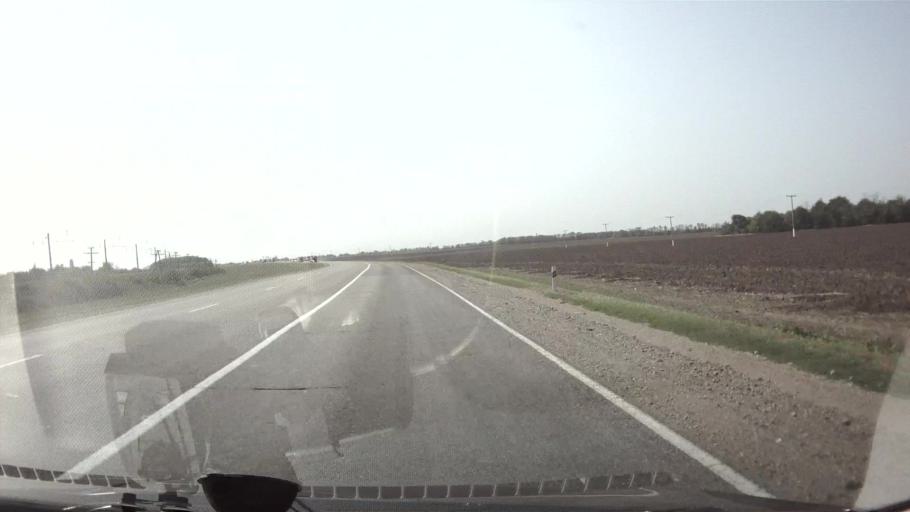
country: RU
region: Krasnodarskiy
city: Ladozhskaya
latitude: 45.3374
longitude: 39.9423
